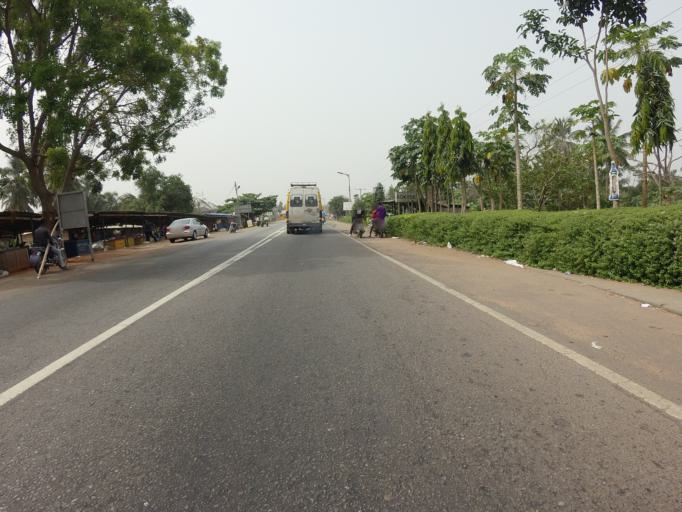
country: GH
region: Volta
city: Anloga
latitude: 5.9934
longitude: 0.5823
